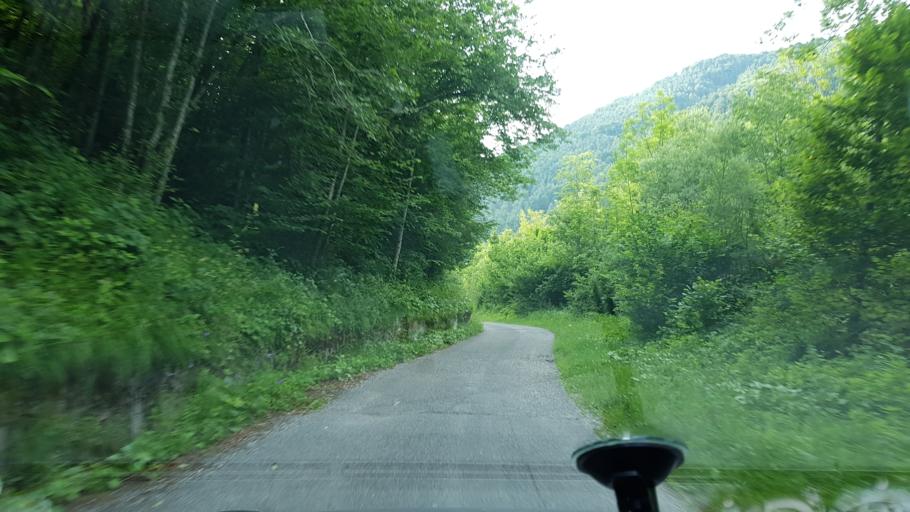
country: IT
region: Friuli Venezia Giulia
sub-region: Provincia di Udine
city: Prato
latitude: 46.3493
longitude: 13.3877
